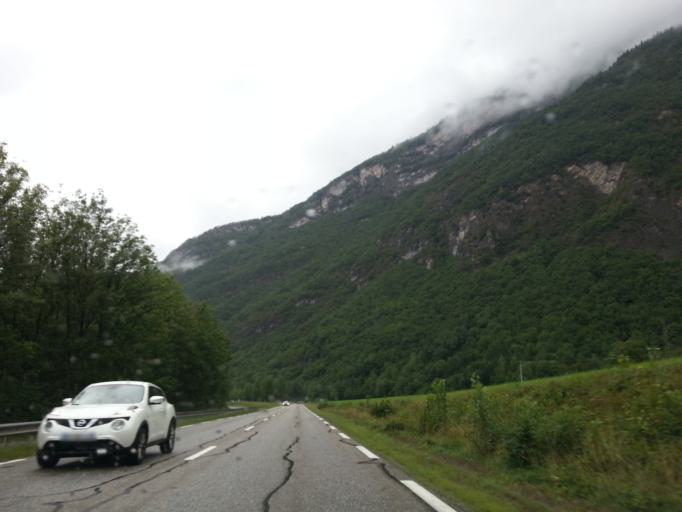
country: FR
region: Rhone-Alpes
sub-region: Departement de la Savoie
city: Ugine
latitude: 45.7641
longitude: 6.3845
